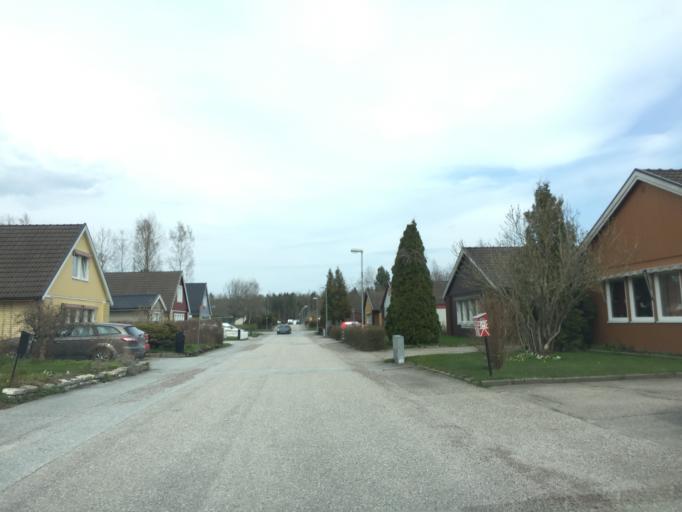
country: SE
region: OErebro
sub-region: Orebro Kommun
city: Orebro
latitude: 59.3122
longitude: 15.1778
